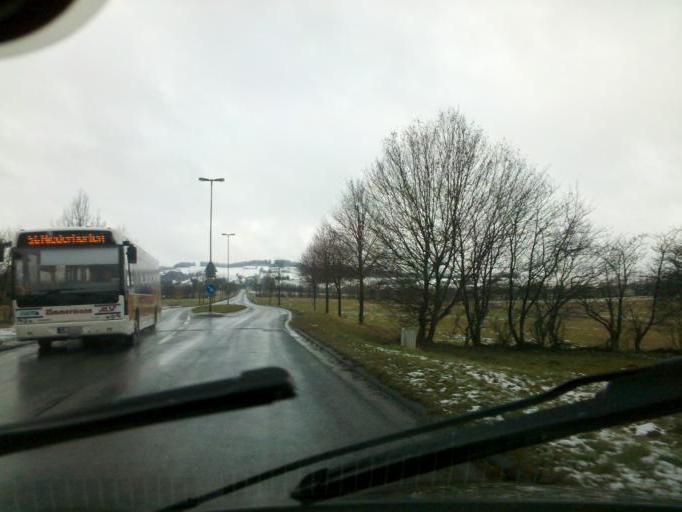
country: DE
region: Hesse
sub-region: Regierungsbezirk Giessen
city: Breidenbach
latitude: 50.8401
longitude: 8.4381
